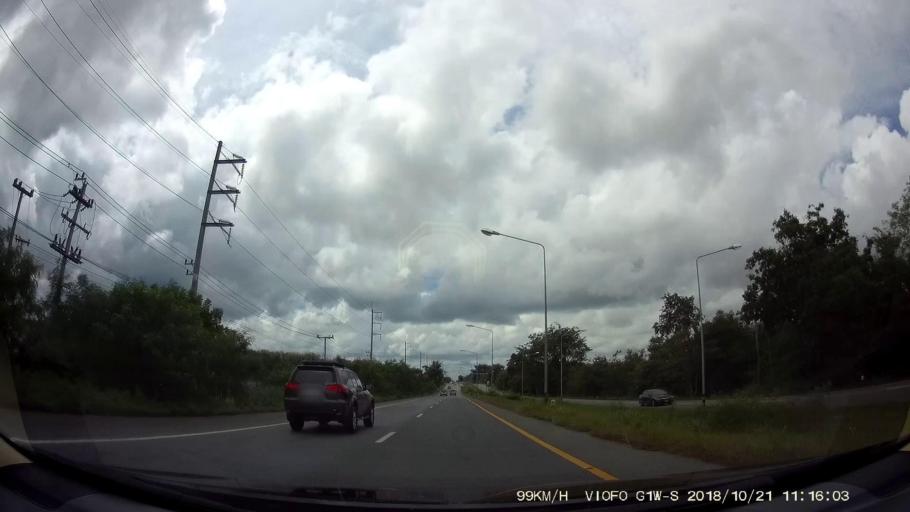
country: TH
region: Chaiyaphum
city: Chaiyaphum
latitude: 15.8896
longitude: 102.1075
